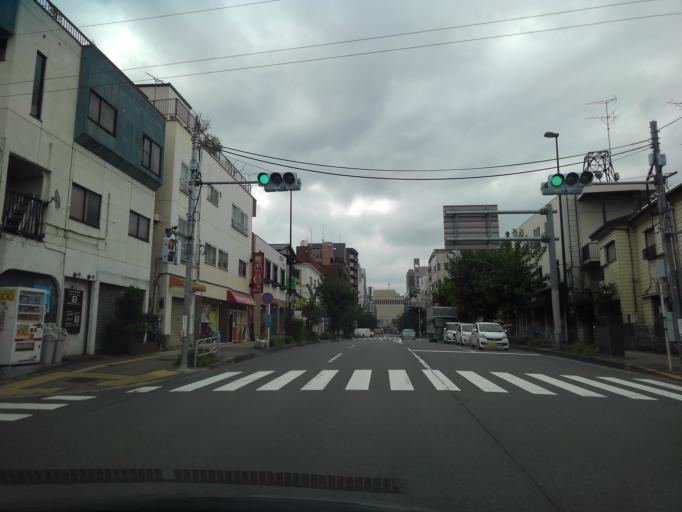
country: JP
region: Tokyo
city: Hachioji
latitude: 35.6625
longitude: 139.3396
